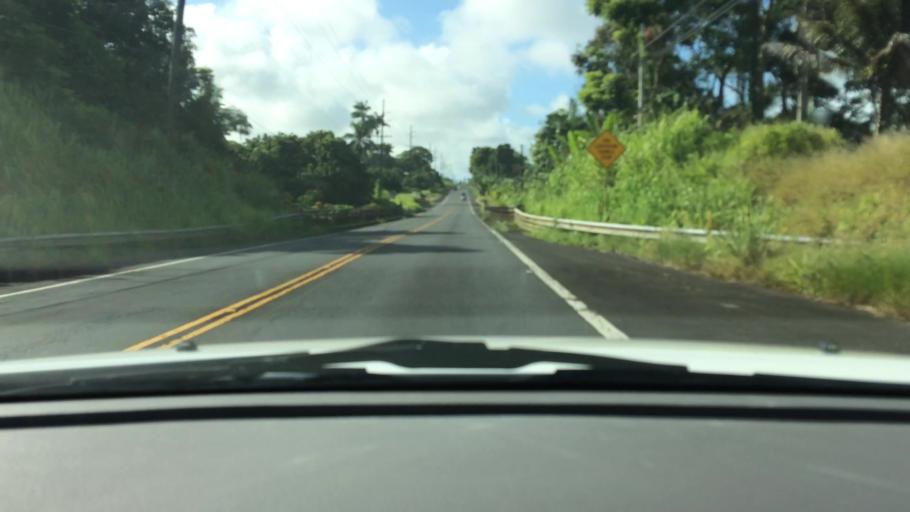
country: US
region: Hawaii
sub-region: Hawaii County
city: Papa'ikou
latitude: 19.7939
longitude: -155.0962
